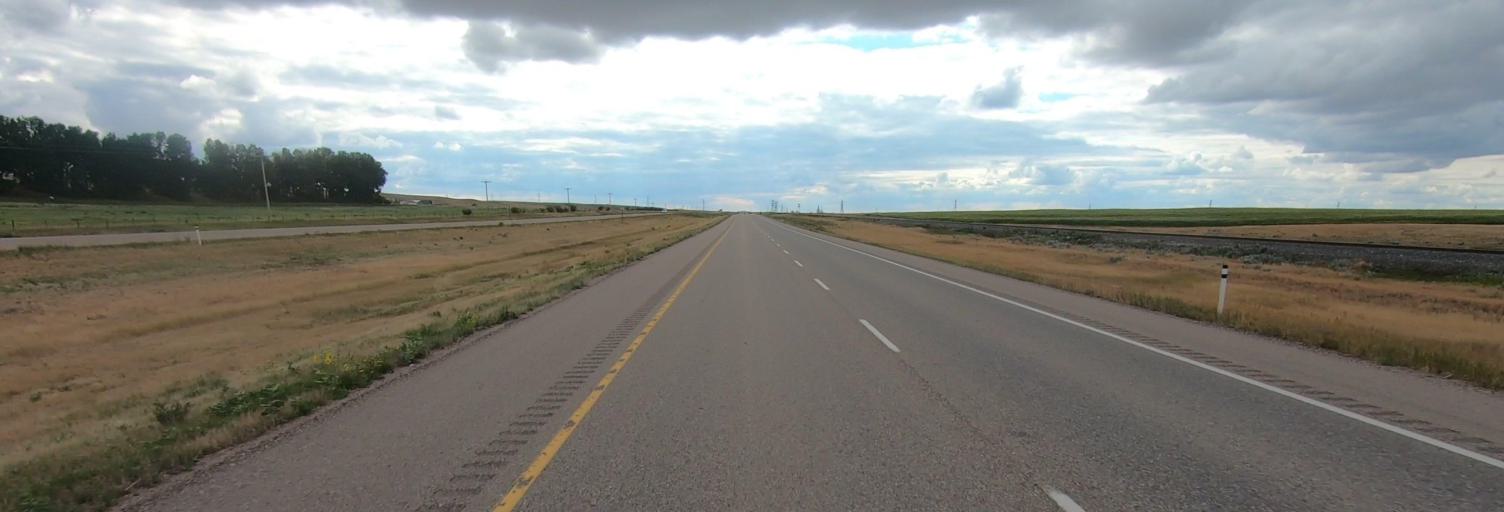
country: CA
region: Alberta
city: Medicine Hat
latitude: 49.9834
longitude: -110.4471
